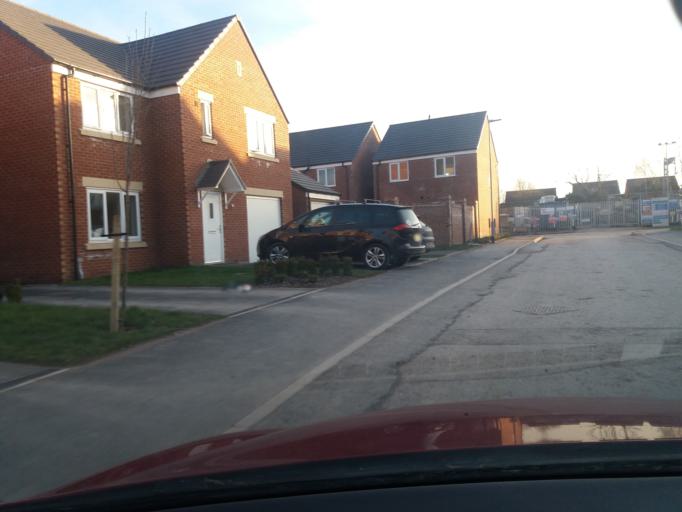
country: GB
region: England
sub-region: Lancashire
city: Euxton
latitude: 53.6762
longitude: -2.6725
